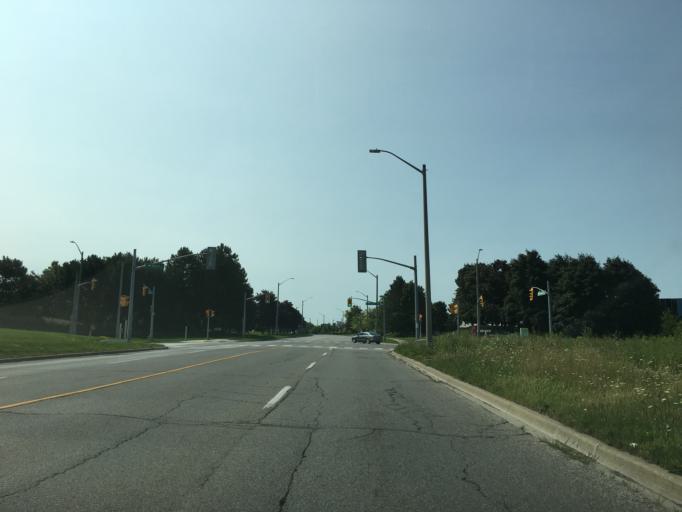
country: CA
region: Ontario
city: Markham
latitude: 43.8363
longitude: -79.3196
